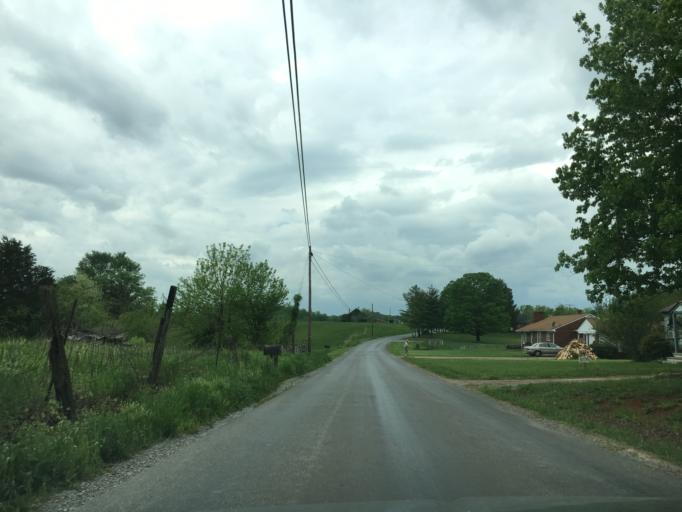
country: US
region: Virginia
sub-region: Campbell County
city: Rustburg
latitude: 37.1667
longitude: -79.0530
